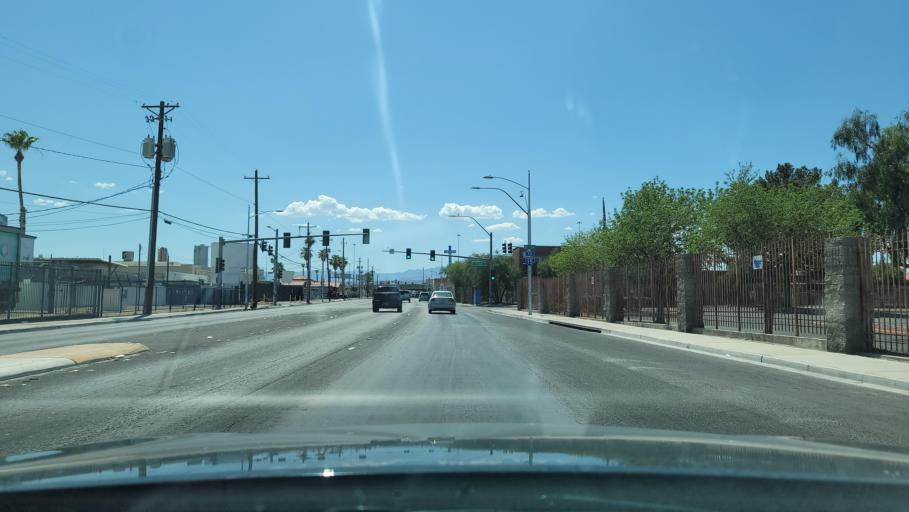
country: US
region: Nevada
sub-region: Clark County
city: Las Vegas
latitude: 36.1773
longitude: -115.1460
